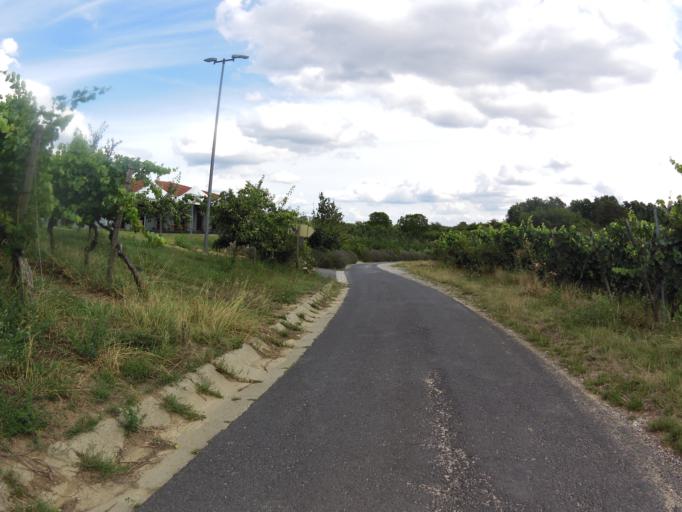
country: DE
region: Bavaria
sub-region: Regierungsbezirk Unterfranken
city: Sommerhausen
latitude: 49.6981
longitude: 10.0357
